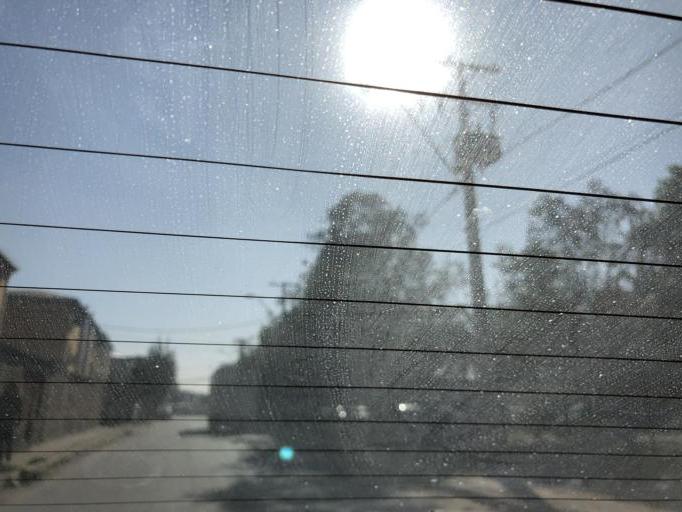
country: CL
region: Santiago Metropolitan
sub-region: Provincia de Santiago
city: La Pintana
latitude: -33.6262
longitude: -70.6264
